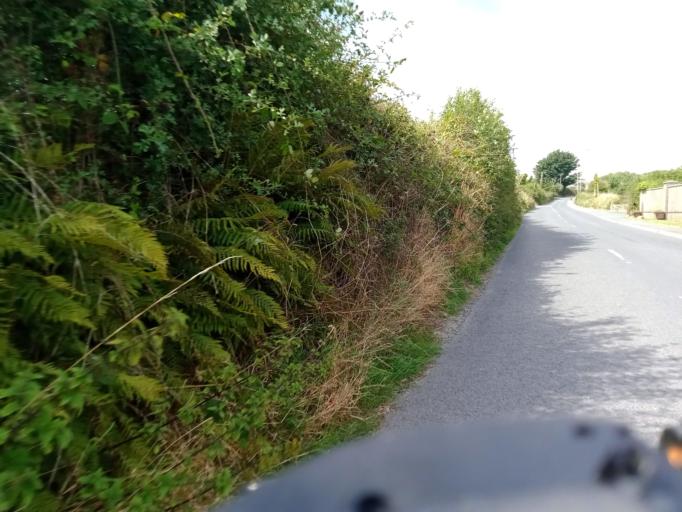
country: IE
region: Munster
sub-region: Waterford
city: Dungarvan
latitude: 52.1320
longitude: -7.4635
